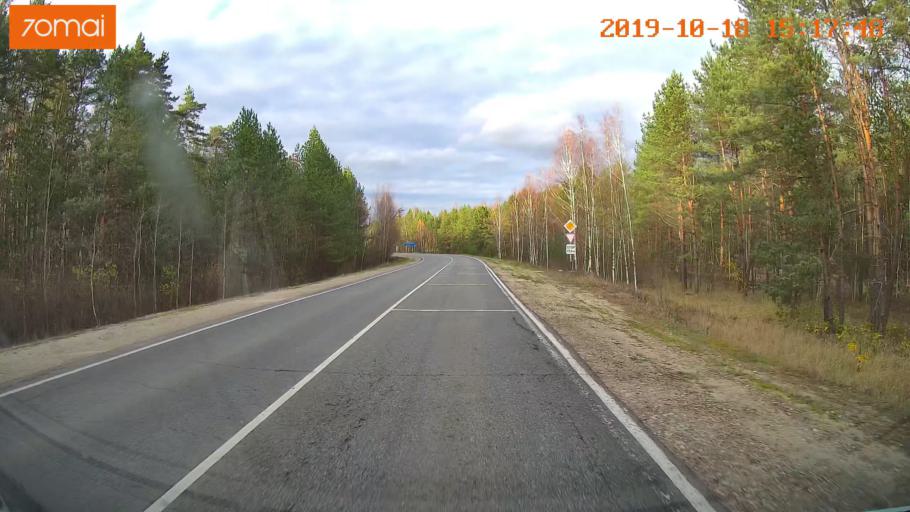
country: RU
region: Vladimir
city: Anopino
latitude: 55.6551
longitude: 40.7273
